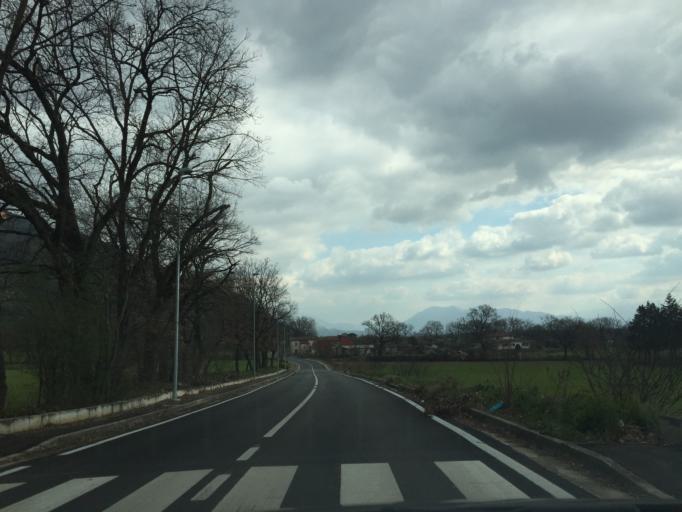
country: IT
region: Latium
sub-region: Provincia di Frosinone
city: Villa Santa Lucia
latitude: 41.4963
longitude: 13.7685
